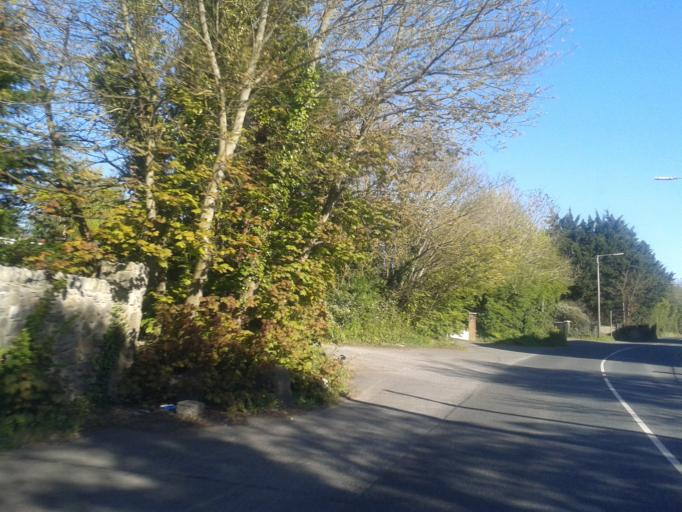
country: IE
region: Leinster
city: Kinsealy-Drinan
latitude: 53.4444
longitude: -6.1965
